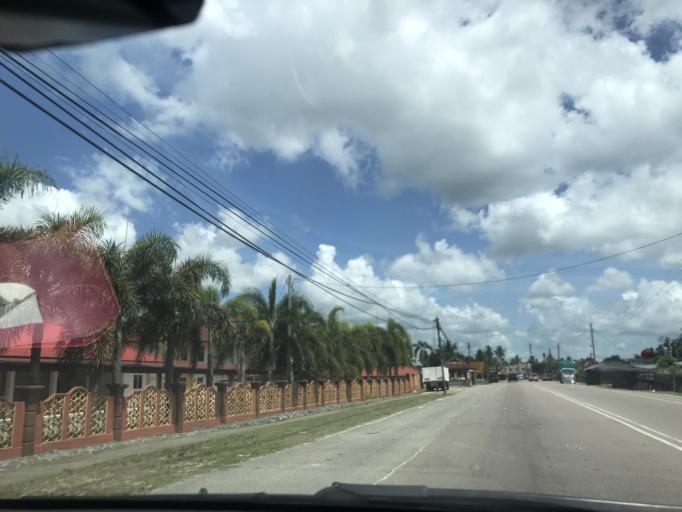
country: MY
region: Kelantan
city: Tumpat
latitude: 6.2181
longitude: 102.1183
